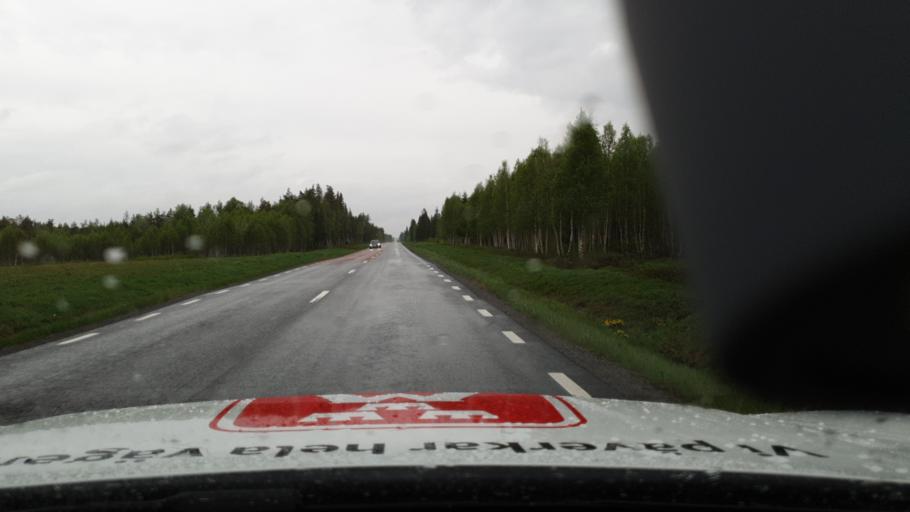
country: SE
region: Jaemtland
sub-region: Stroemsunds Kommun
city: Stroemsund
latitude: 63.7967
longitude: 15.5153
